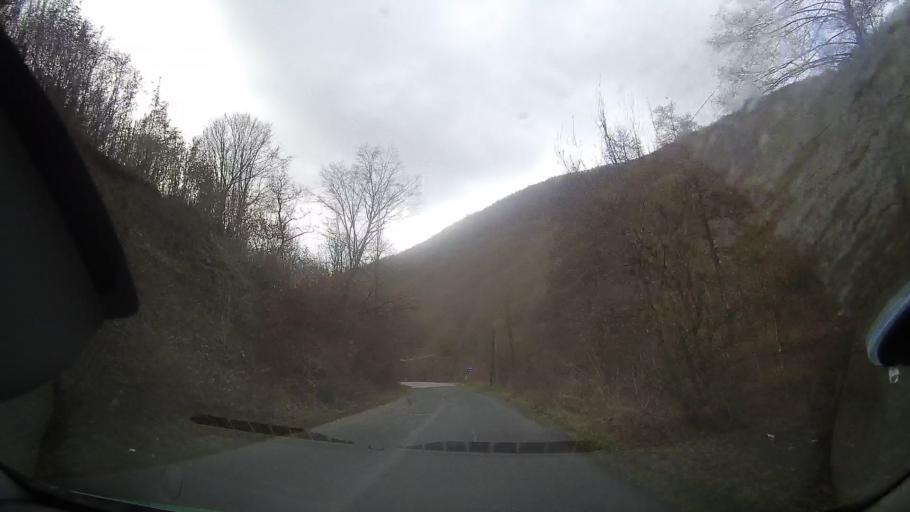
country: RO
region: Alba
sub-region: Comuna Rimetea
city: Rimetea
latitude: 46.4942
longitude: 23.5807
